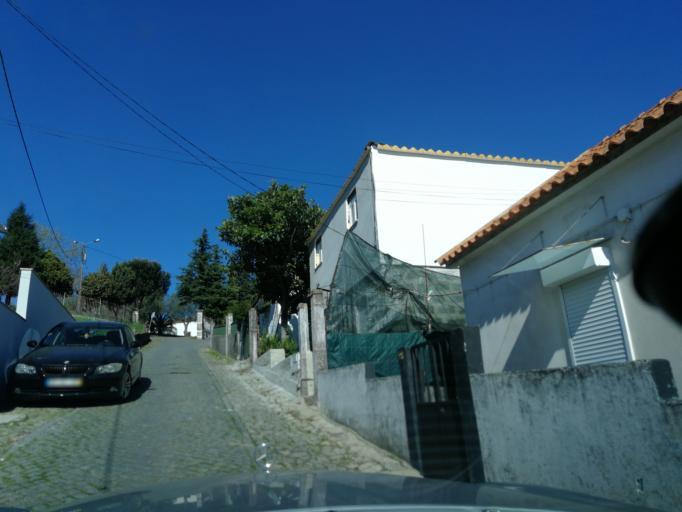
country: PT
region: Braga
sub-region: Braga
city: Braga
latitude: 41.5418
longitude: -8.4444
